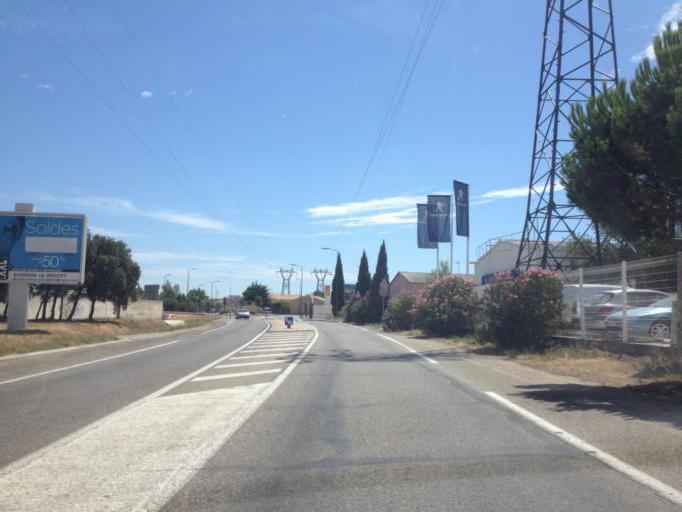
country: FR
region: Provence-Alpes-Cote d'Azur
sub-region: Departement du Vaucluse
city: Sorgues
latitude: 44.0154
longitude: 4.8837
